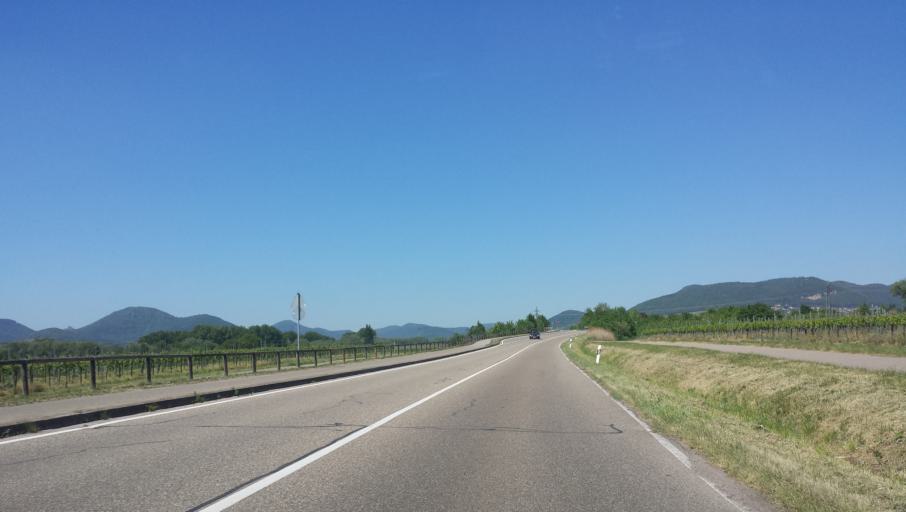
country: DE
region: Rheinland-Pfalz
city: Landau in der Pfalz
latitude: 49.2063
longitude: 8.0988
